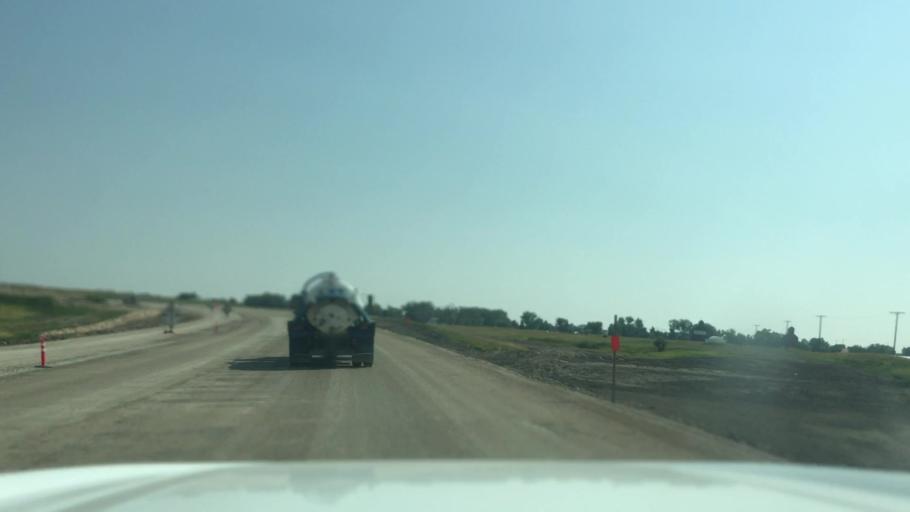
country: US
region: Montana
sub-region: Judith Basin County
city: Stanford
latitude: 47.0084
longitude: -109.8719
